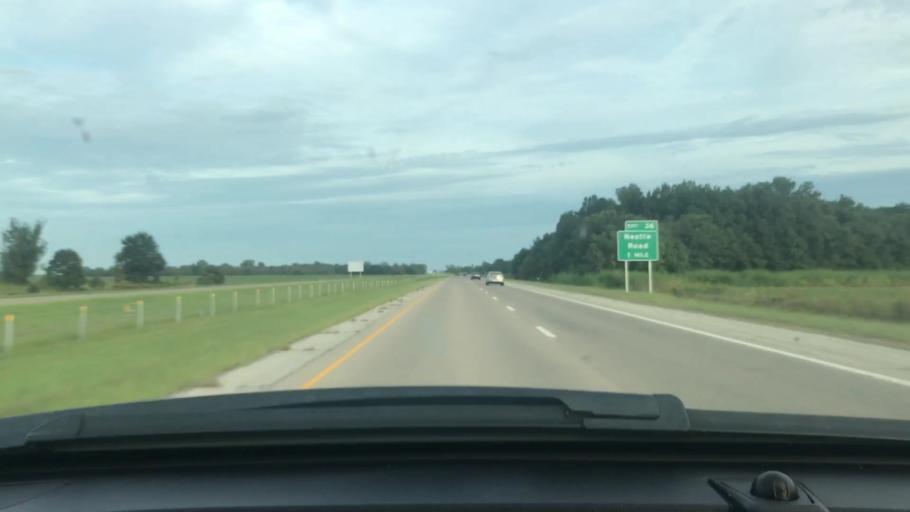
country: US
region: Arkansas
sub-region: Craighead County
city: Bay
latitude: 35.7903
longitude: -90.6089
